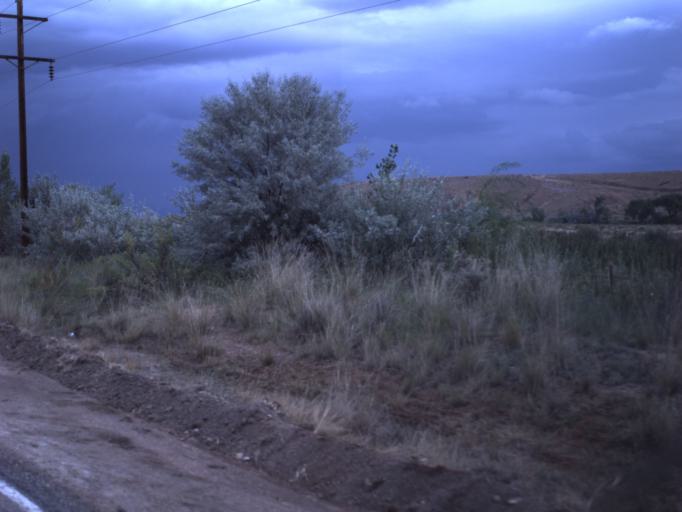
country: US
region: Utah
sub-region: Duchesne County
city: Roosevelt
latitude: 40.3406
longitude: -110.0250
